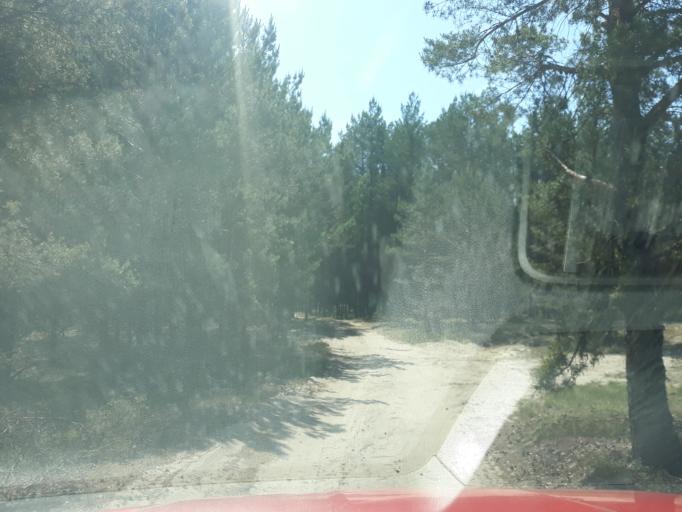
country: PL
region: Pomeranian Voivodeship
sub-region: Powiat chojnicki
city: Chojnice
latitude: 53.8708
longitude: 17.5408
